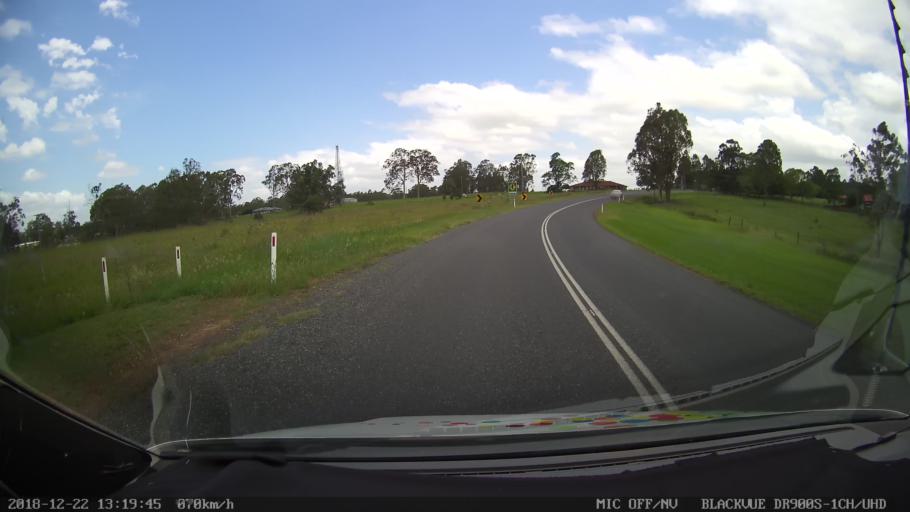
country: AU
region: New South Wales
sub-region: Clarence Valley
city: South Grafton
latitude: -29.7595
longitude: 152.9304
